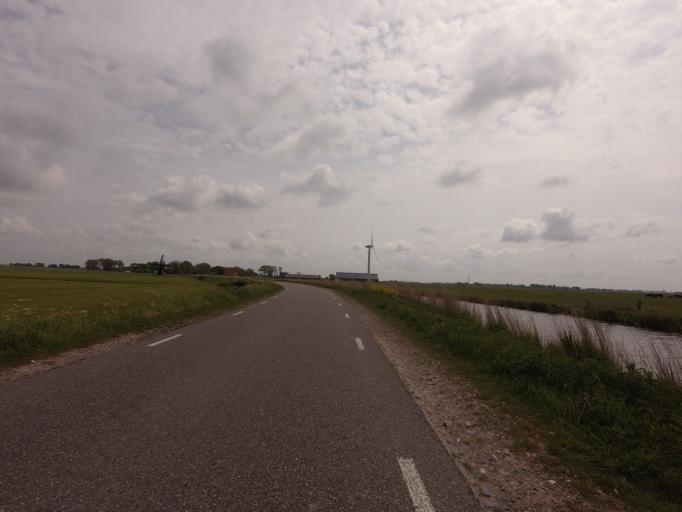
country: NL
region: Friesland
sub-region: Sudwest Fryslan
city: Bolsward
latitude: 53.1006
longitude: 5.5162
